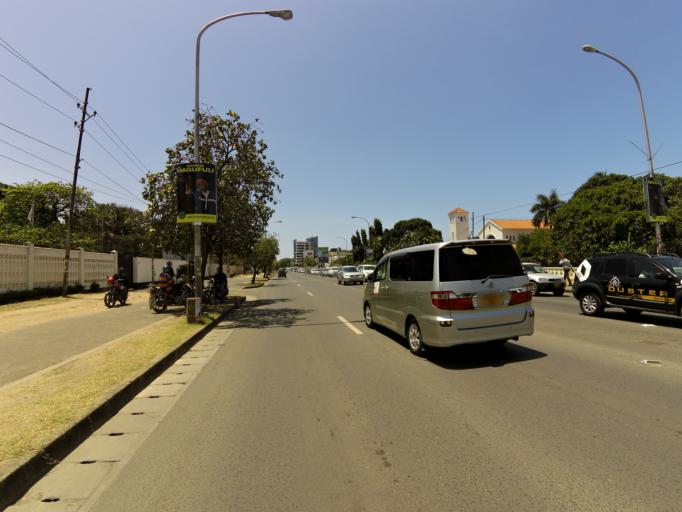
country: TZ
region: Dar es Salaam
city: Dar es Salaam
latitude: -6.8090
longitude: 39.2866
